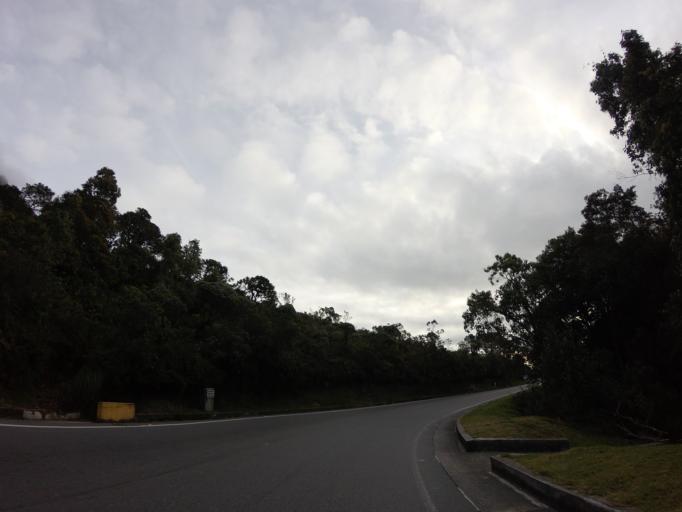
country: CO
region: Tolima
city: Herveo
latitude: 5.0863
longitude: -75.2806
